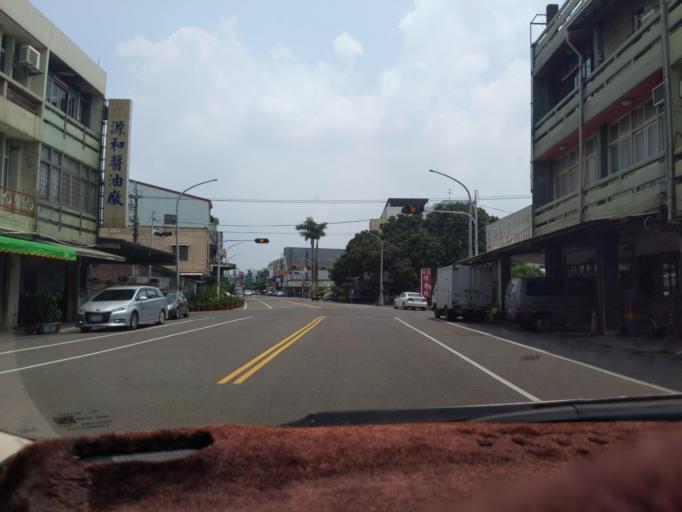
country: TW
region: Taiwan
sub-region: Yunlin
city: Douliu
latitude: 23.8014
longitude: 120.4648
